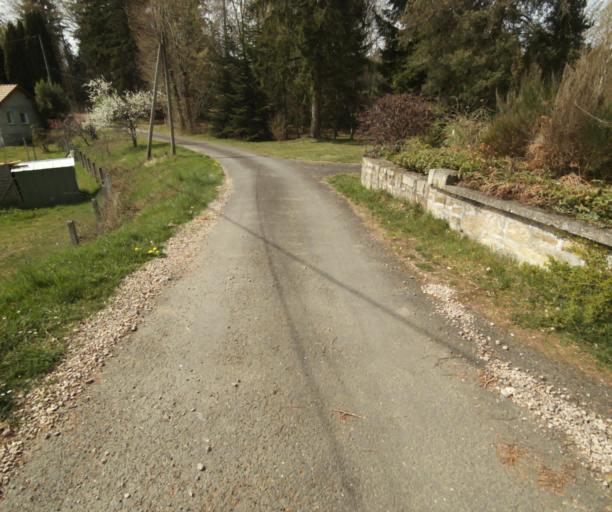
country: FR
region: Limousin
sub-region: Departement de la Correze
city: Naves
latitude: 45.3315
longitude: 1.7697
